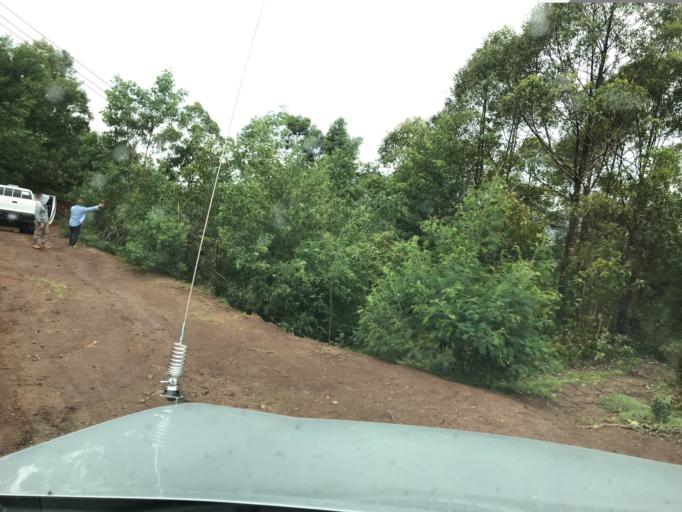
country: TL
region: Ainaro
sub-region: Ainaro
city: Ainaro
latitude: -8.8783
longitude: 125.5532
